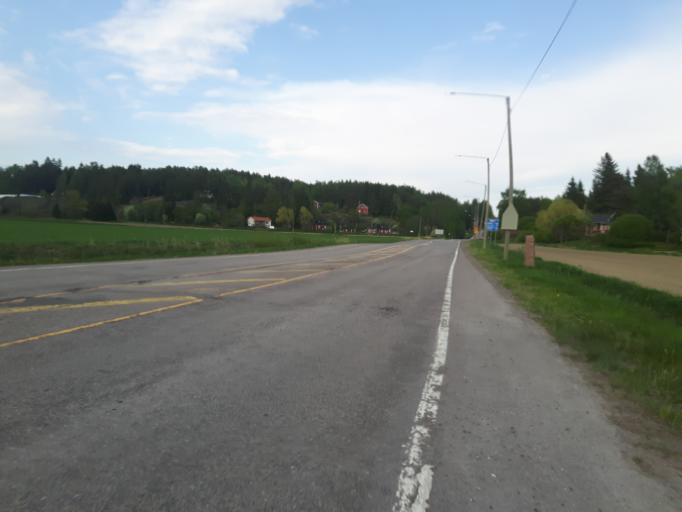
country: FI
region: Uusimaa
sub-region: Loviisa
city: Perna
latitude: 60.4927
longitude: 25.8928
